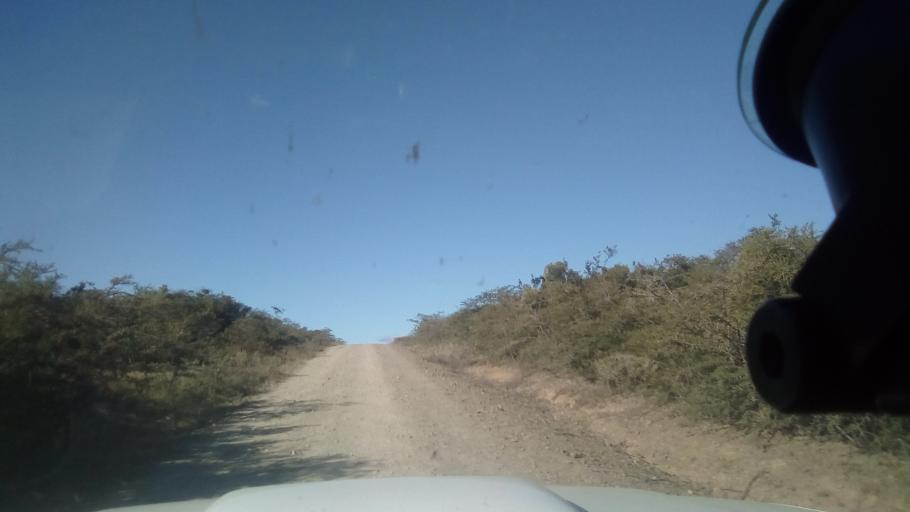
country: ZA
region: Eastern Cape
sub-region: Buffalo City Metropolitan Municipality
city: Bhisho
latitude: -32.7528
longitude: 27.3496
